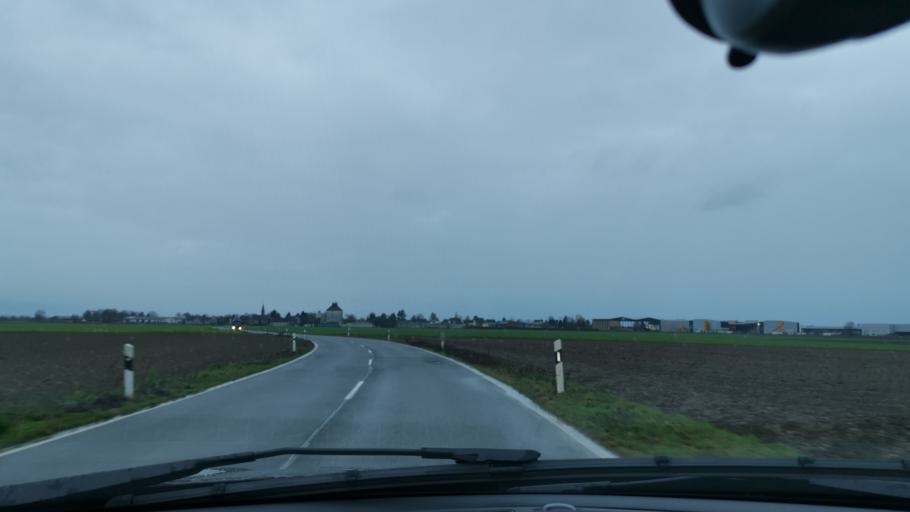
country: DE
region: North Rhine-Westphalia
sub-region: Regierungsbezirk Koln
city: Titz
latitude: 50.9883
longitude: 6.4483
